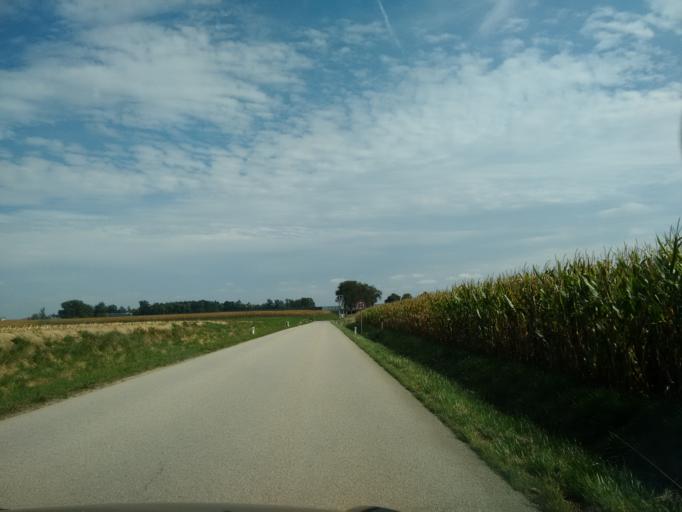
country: AT
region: Upper Austria
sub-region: Wels-Land
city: Marchtrenk
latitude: 48.1260
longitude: 14.1106
